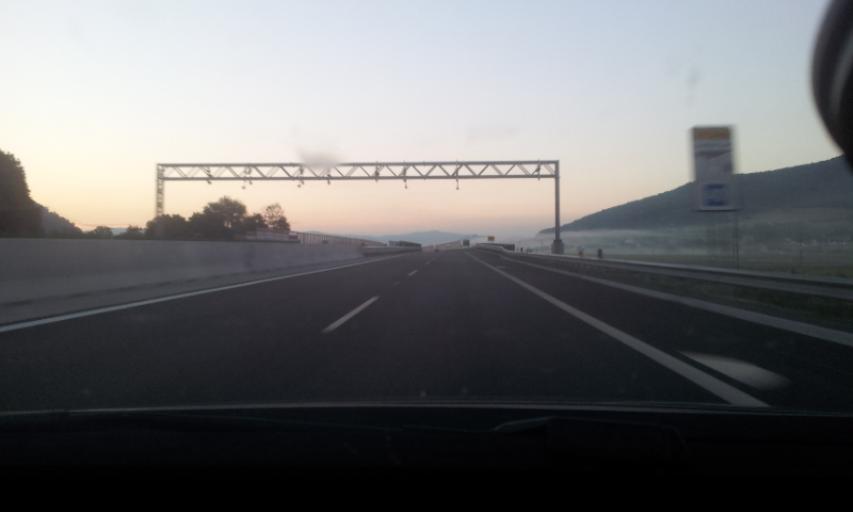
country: SK
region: Banskobystricky
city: Detva
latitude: 48.5414
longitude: 19.3616
